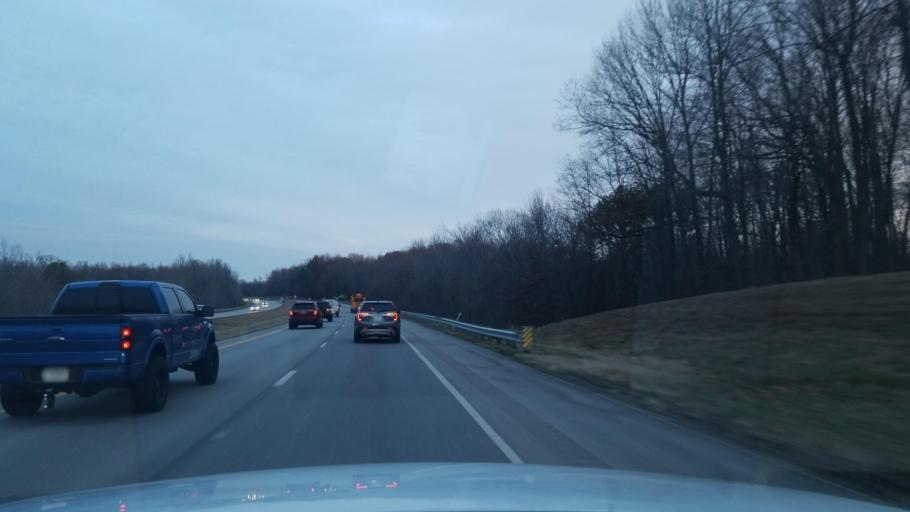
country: US
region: Indiana
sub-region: Vanderburgh County
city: Evansville
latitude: 37.9491
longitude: -87.7026
